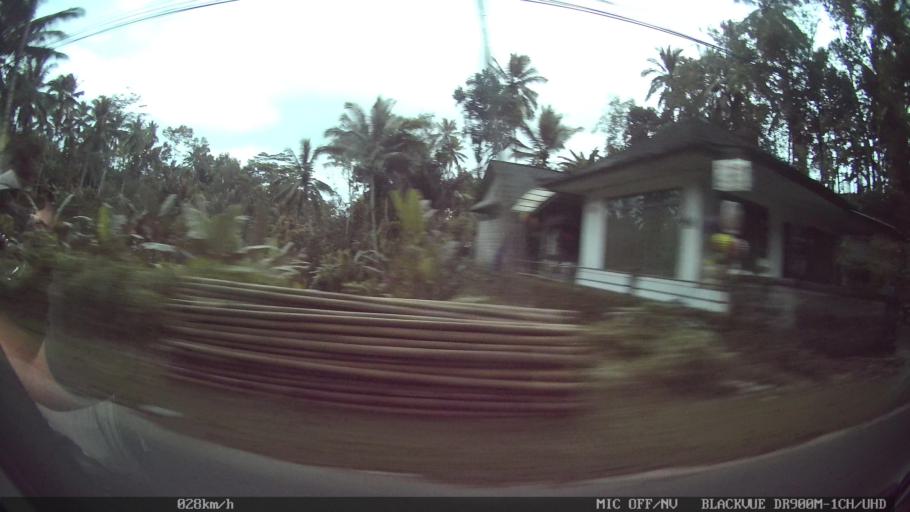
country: ID
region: Bali
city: Tegalalang
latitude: -8.4466
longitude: 115.2734
